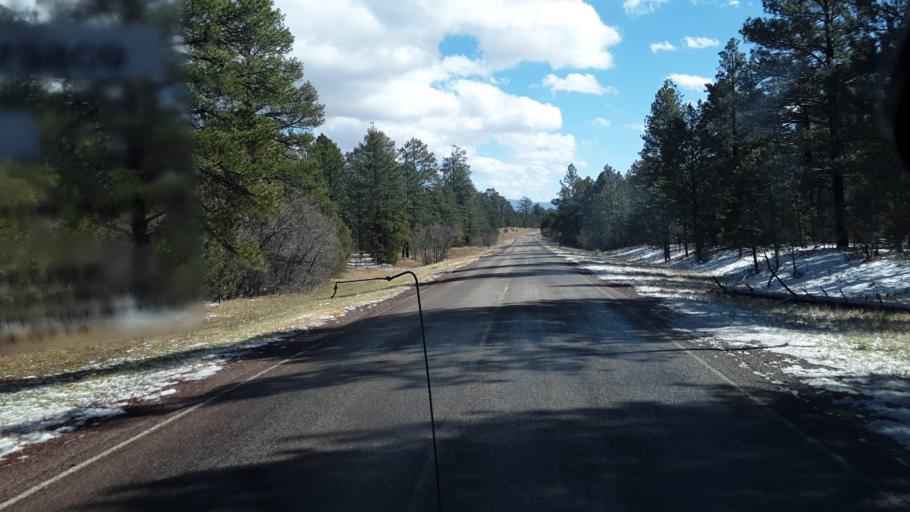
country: US
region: New Mexico
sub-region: Rio Arriba County
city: Santa Teresa
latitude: 36.1990
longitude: -106.7534
